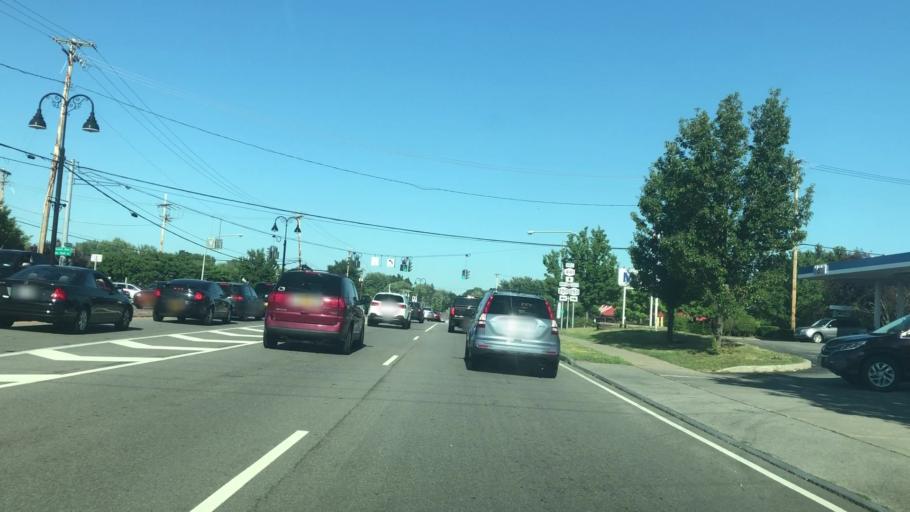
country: US
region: New York
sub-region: Monroe County
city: Fairport
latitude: 43.1307
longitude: -77.4424
